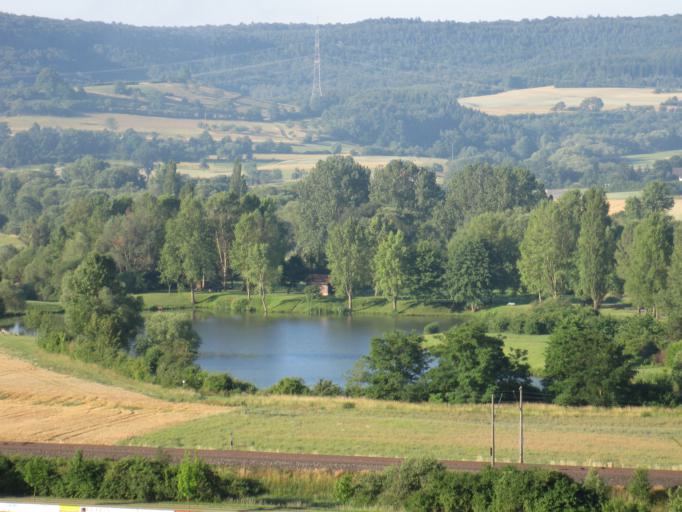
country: DE
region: Bavaria
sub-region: Regierungsbezirk Unterfranken
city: Zeil
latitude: 49.9999
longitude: 10.6244
